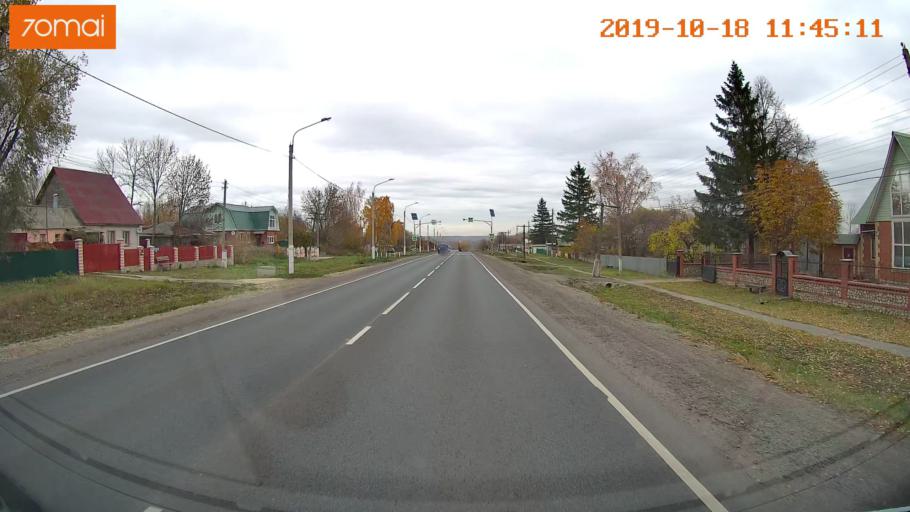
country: RU
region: Rjazan
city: Mikhaylov
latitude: 54.2084
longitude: 38.9670
